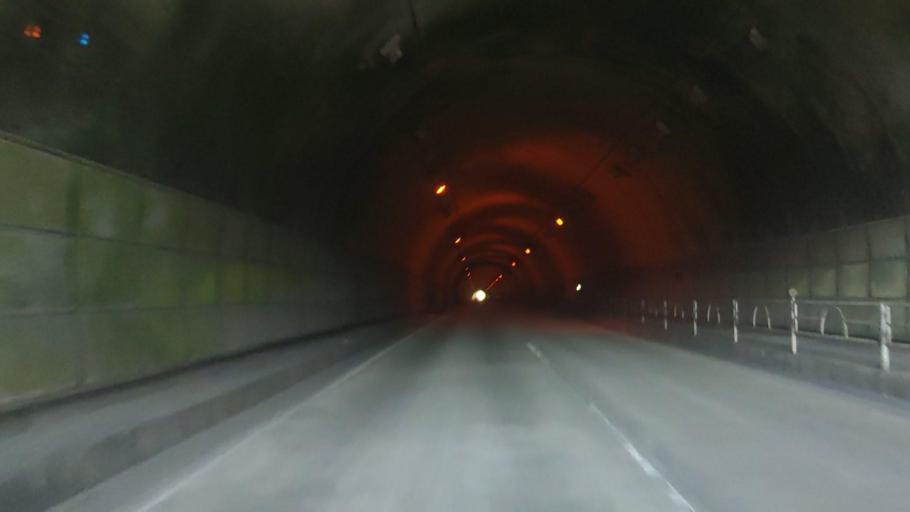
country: JP
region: Miyazaki
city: Nobeoka
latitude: 32.6709
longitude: 131.7682
